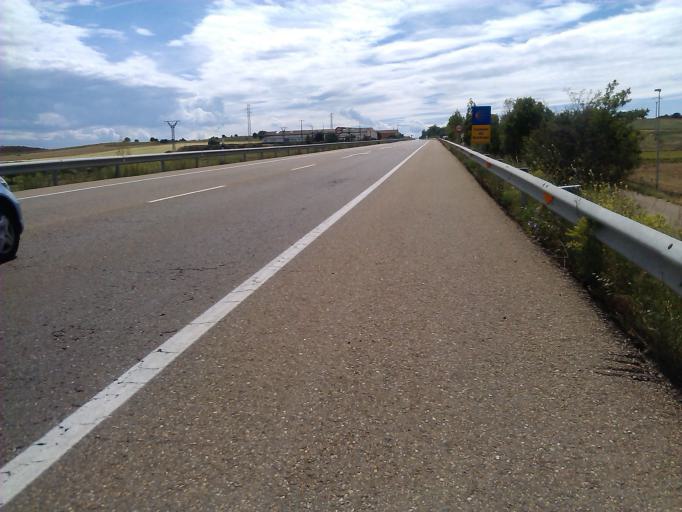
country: ES
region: Castille and Leon
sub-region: Provincia de Leon
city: Villarejo de Orbigo
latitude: 42.4507
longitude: -5.9280
